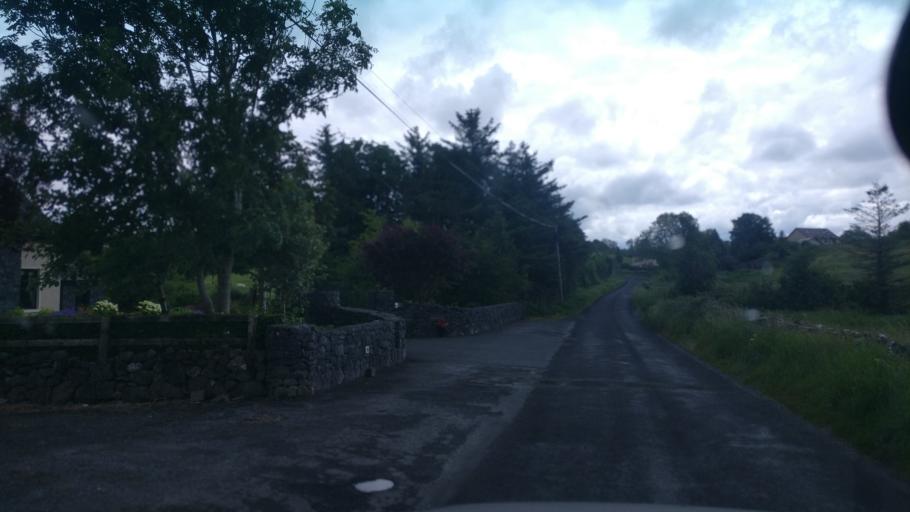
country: IE
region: Connaught
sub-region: County Galway
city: Loughrea
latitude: 53.1694
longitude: -8.5698
